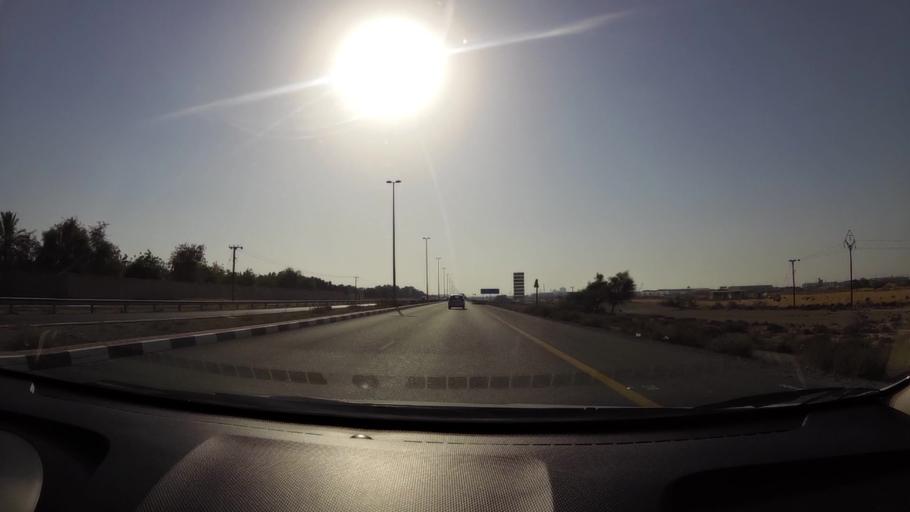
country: AE
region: Umm al Qaywayn
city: Umm al Qaywayn
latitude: 25.4314
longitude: 55.5780
